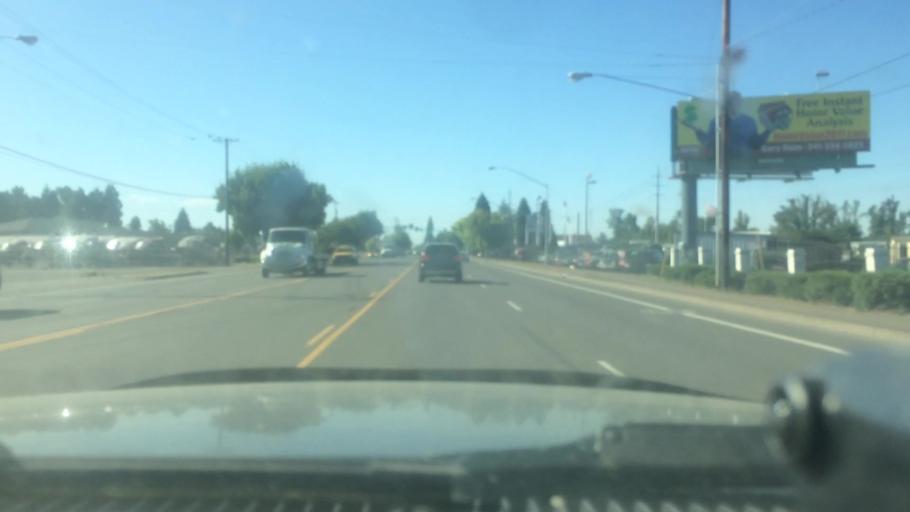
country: US
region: Oregon
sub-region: Lane County
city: Eugene
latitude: 44.0789
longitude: -123.1504
